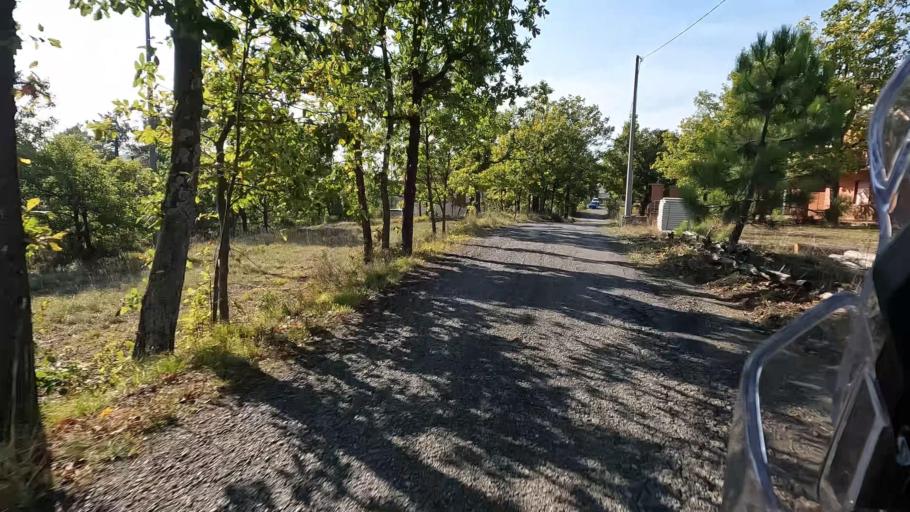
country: IT
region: Liguria
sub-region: Provincia di Savona
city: Urbe
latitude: 44.5274
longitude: 8.5394
